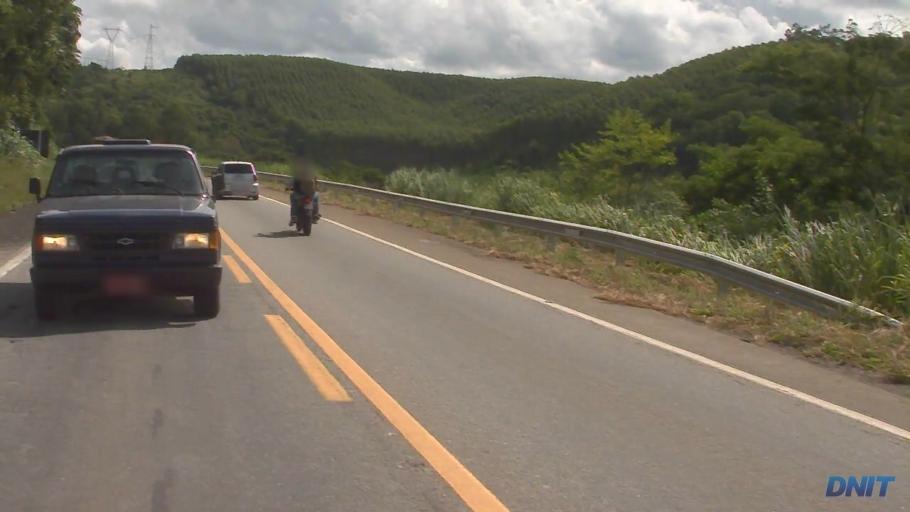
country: BR
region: Minas Gerais
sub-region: Ipaba
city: Ipaba
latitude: -19.3983
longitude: -42.4838
